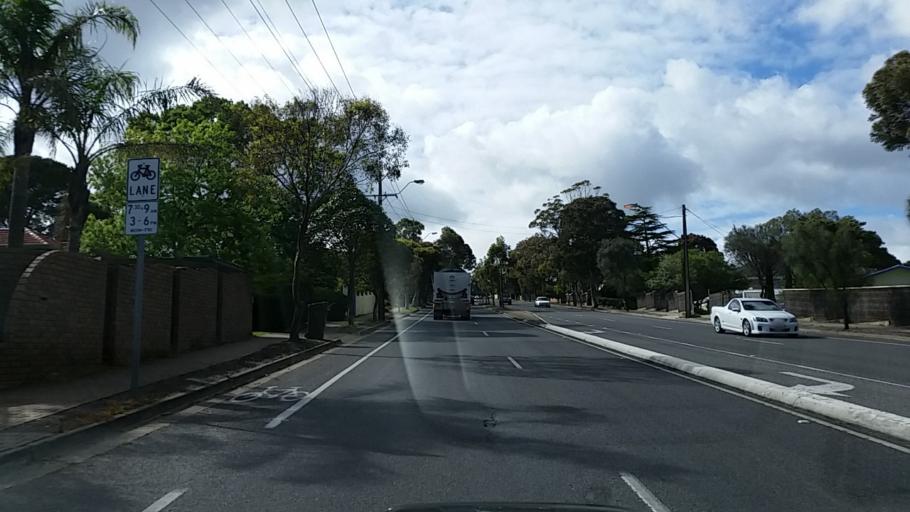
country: AU
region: South Australia
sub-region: Marion
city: Marion
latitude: -35.0197
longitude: 138.5810
